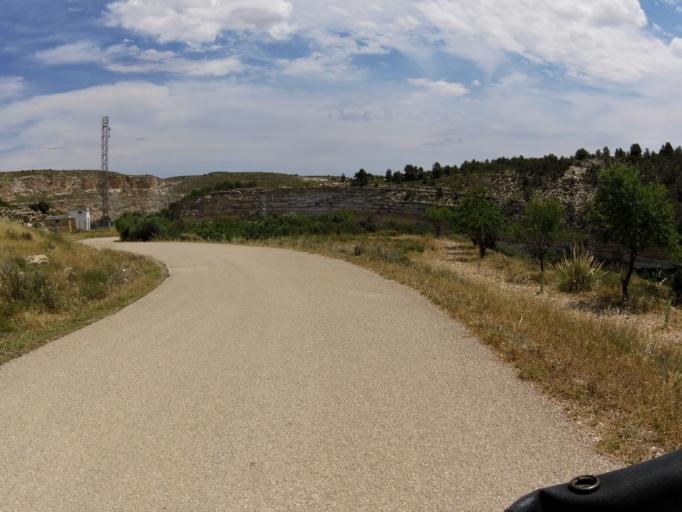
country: ES
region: Castille-La Mancha
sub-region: Provincia de Albacete
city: Valdeganga
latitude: 39.1607
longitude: -1.6108
